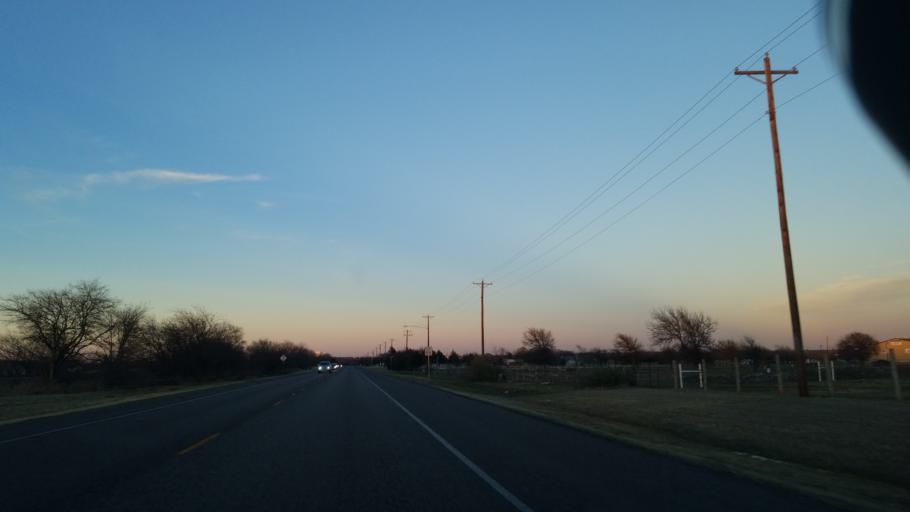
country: US
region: Texas
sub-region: Denton County
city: Argyle
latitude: 33.1510
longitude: -97.1671
